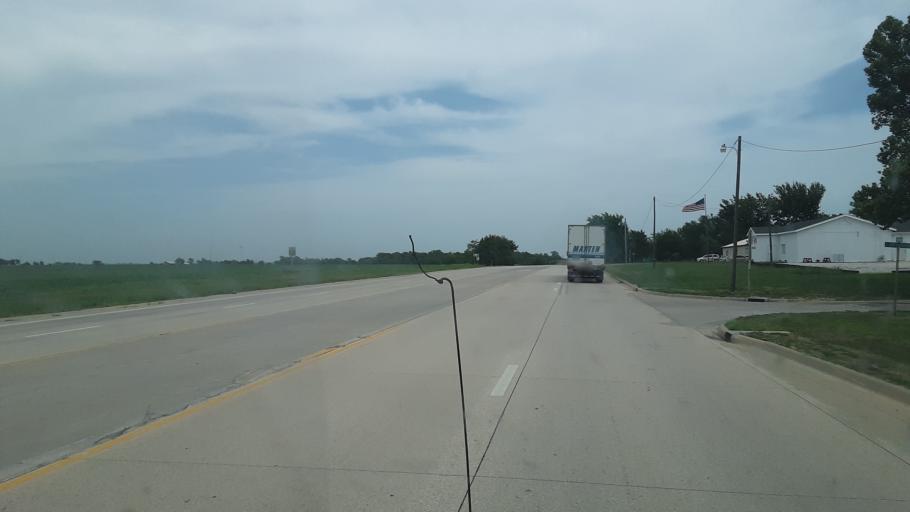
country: US
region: Kansas
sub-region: Allen County
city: Iola
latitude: 37.9221
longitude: -95.2984
